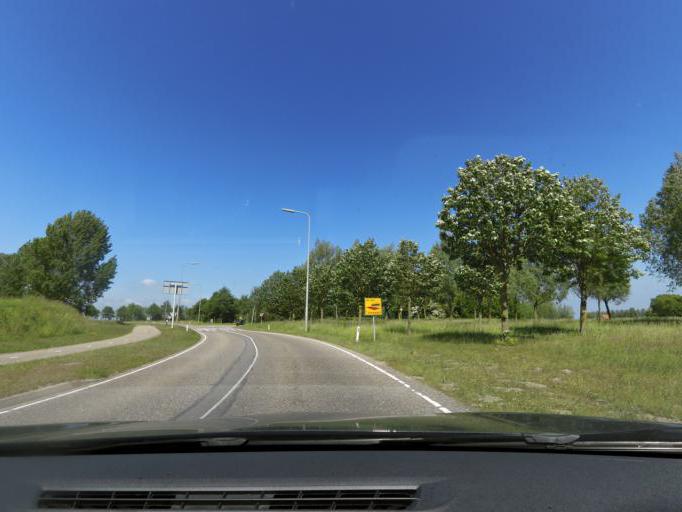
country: NL
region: South Holland
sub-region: Gemeente Goeree-Overflakkee
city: Dirksland
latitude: 51.7769
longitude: 4.0748
